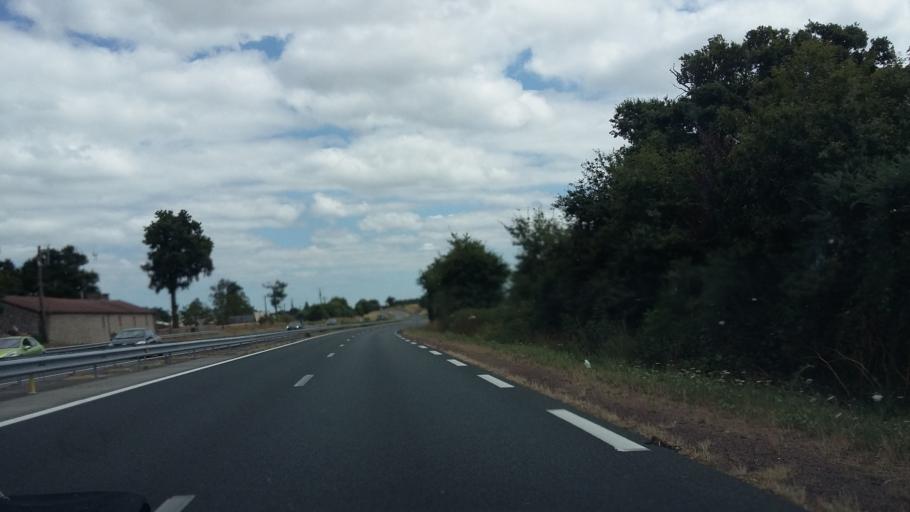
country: FR
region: Pays de la Loire
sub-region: Departement de la Vendee
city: Bournezeau
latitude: 46.6415
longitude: -1.1922
